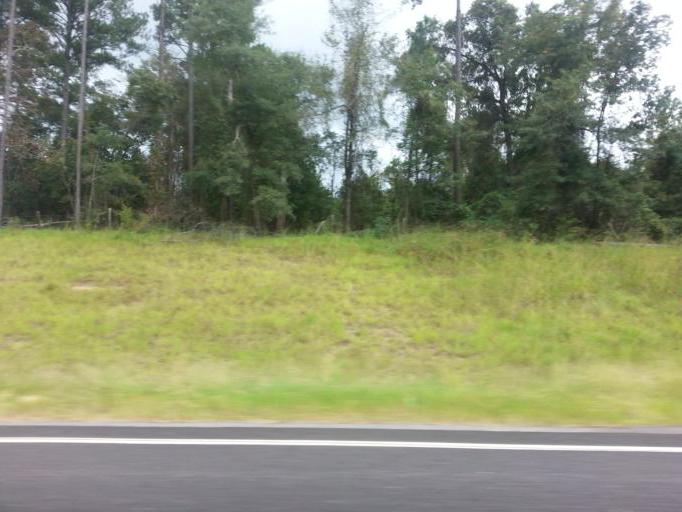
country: US
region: Alabama
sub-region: Conecuh County
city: Evergreen
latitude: 31.3309
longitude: -87.1242
